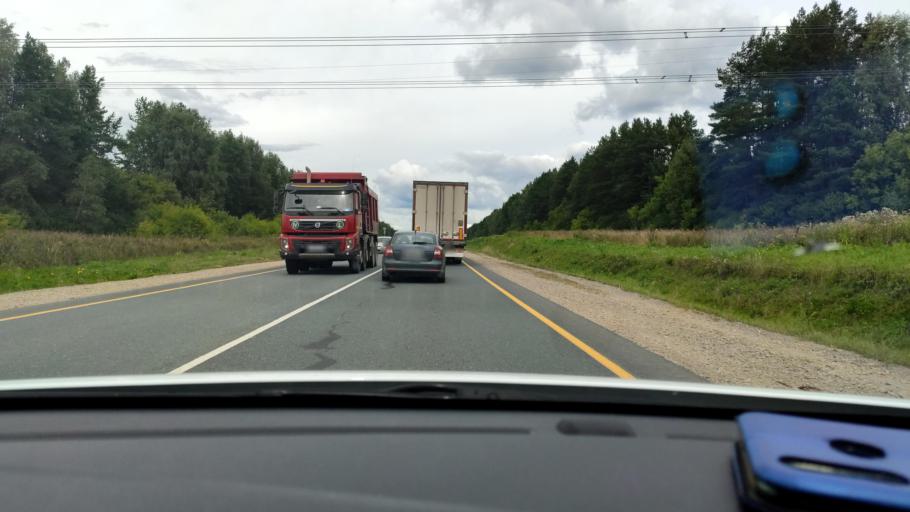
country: RU
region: Mariy-El
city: Pomary
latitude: 55.9827
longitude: 48.3757
